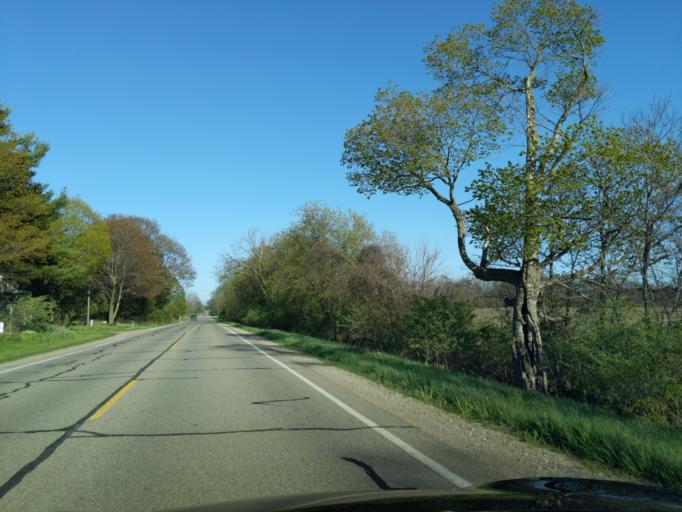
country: US
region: Michigan
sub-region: Eaton County
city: Grand Ledge
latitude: 42.8122
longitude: -84.8108
